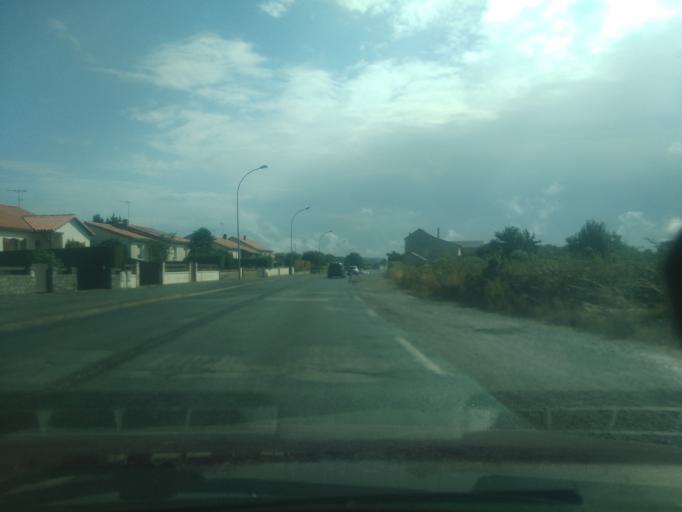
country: FR
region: Poitou-Charentes
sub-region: Departement des Deux-Sevres
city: Parthenay
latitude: 46.6396
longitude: -0.2401
